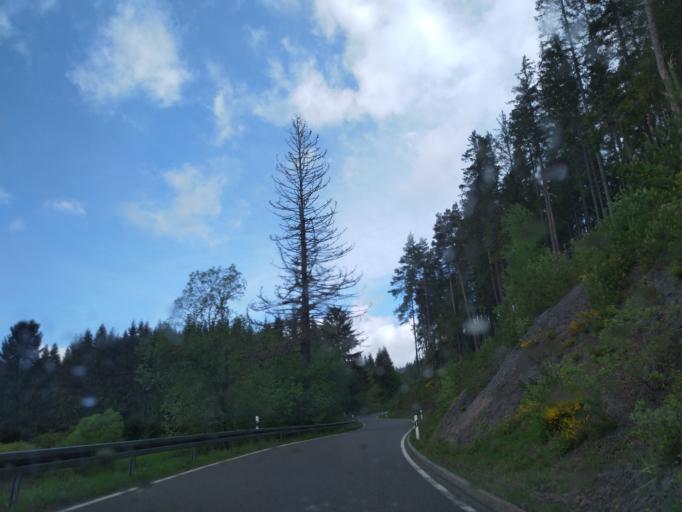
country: DE
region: Baden-Wuerttemberg
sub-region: Freiburg Region
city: Friedenweiler
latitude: 47.9239
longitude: 8.2579
